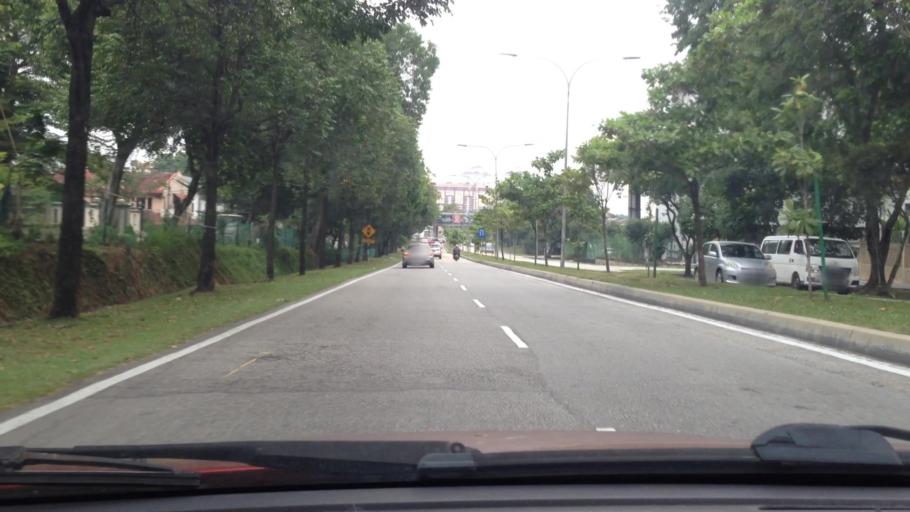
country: MY
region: Selangor
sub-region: Petaling
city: Petaling Jaya
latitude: 3.0948
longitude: 101.6072
